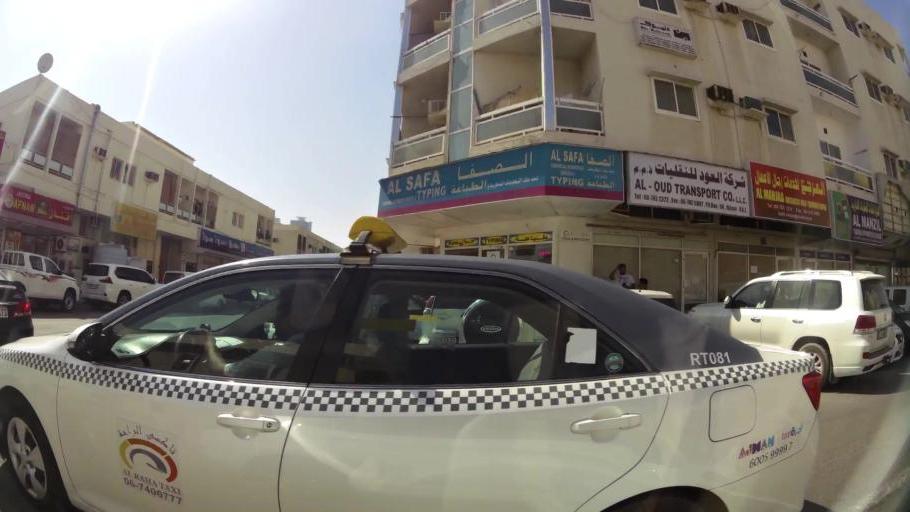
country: AE
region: Ajman
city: Ajman
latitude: 25.4071
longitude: 55.4450
